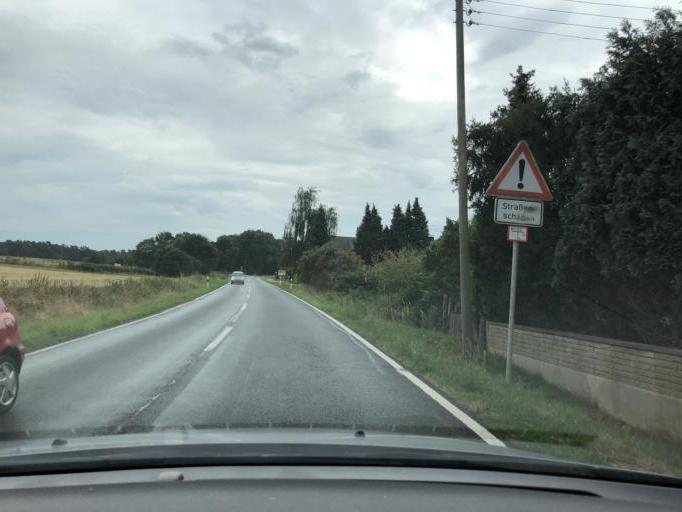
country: DE
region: North Rhine-Westphalia
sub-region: Regierungsbezirk Dusseldorf
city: Schermbeck
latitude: 51.6434
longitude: 6.8962
